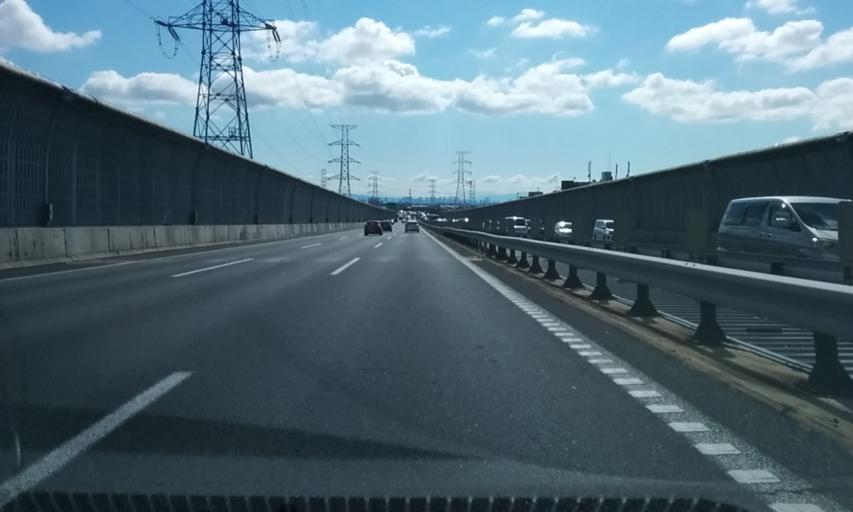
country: JP
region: Hyogo
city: Takarazuka
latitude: 34.8135
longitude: 135.3598
